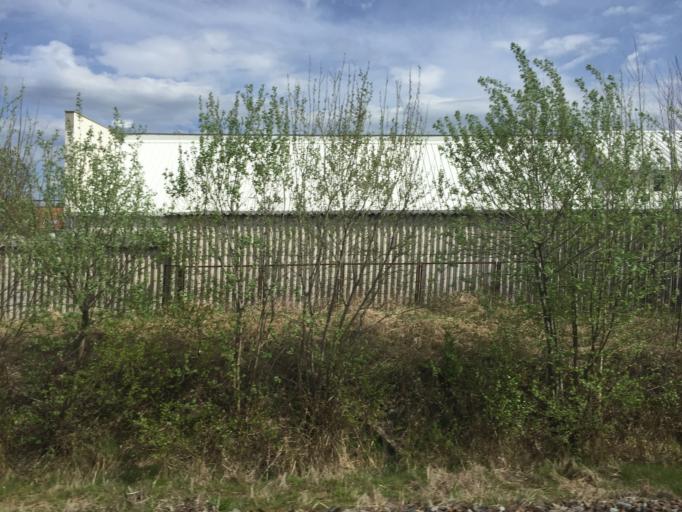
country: DE
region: Saxony
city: Reichenbach
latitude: 51.1344
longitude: 14.8020
